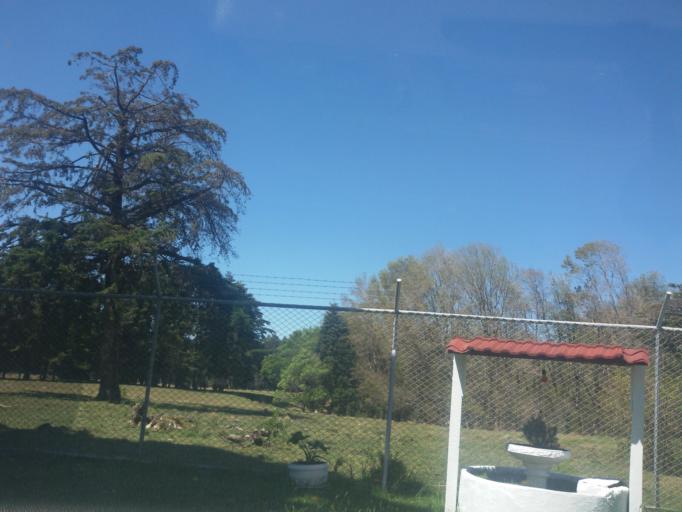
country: CR
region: Heredia
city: San Josecito
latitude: 10.0778
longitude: -84.0934
